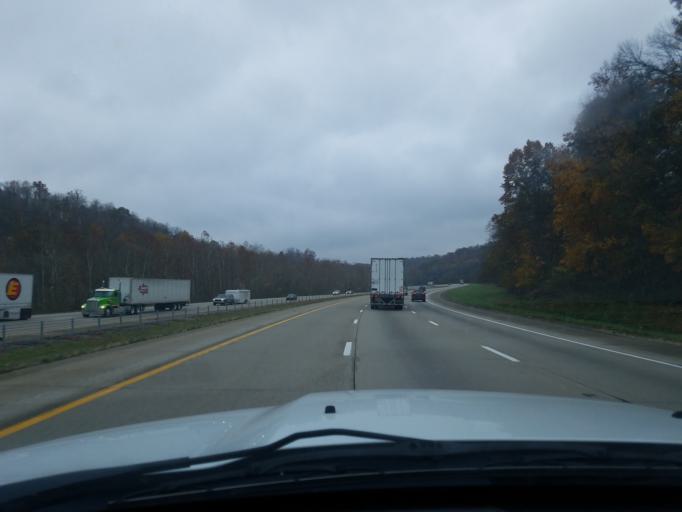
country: US
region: Kentucky
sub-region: Bullitt County
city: Lebanon Junction
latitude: 37.7716
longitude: -85.7840
